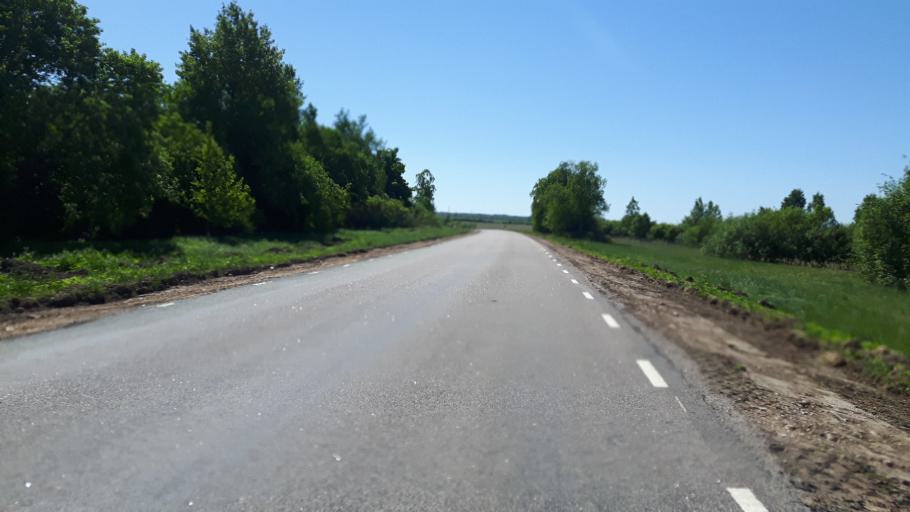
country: EE
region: Ida-Virumaa
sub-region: Narva-Joesuu linn
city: Narva-Joesuu
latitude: 59.3893
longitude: 27.9211
